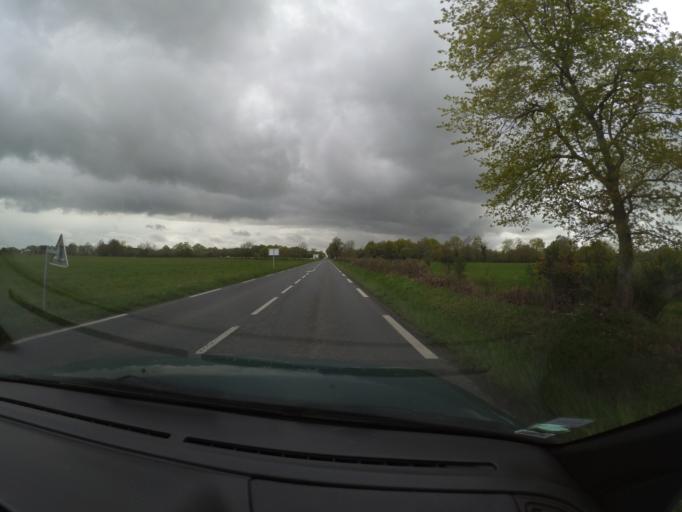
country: FR
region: Pays de la Loire
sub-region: Departement de la Loire-Atlantique
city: La Remaudiere
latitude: 47.2177
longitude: -1.2356
